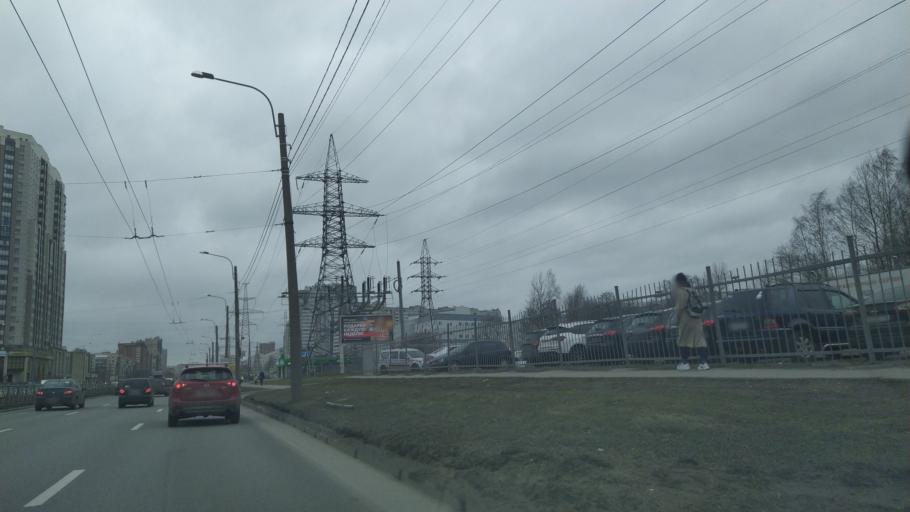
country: RU
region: Leningrad
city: Chernaya Rechka
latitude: 60.0021
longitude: 30.3058
